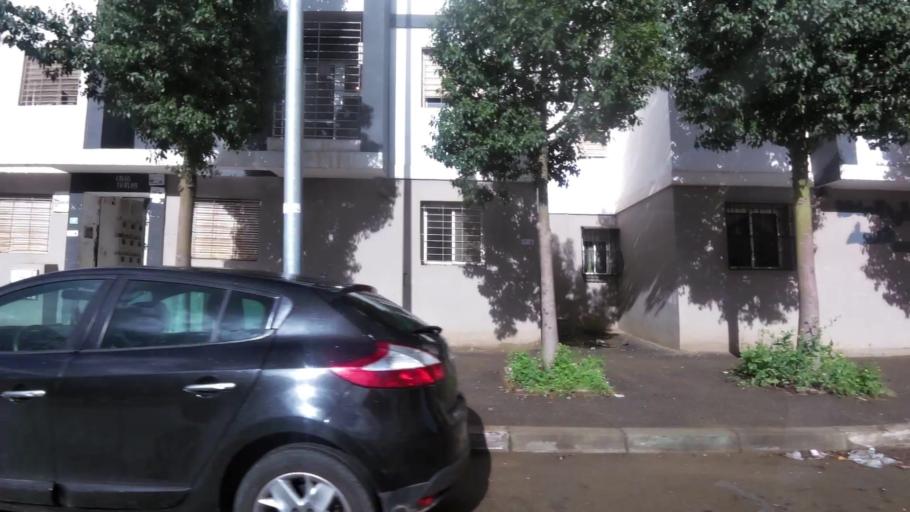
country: MA
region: Grand Casablanca
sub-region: Casablanca
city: Casablanca
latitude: 33.5429
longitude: -7.6929
